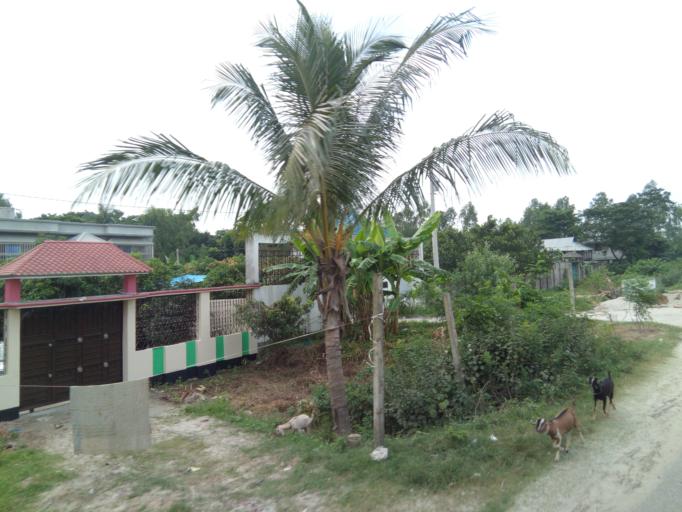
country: BD
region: Dhaka
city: Dohar
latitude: 23.5511
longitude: 90.3001
